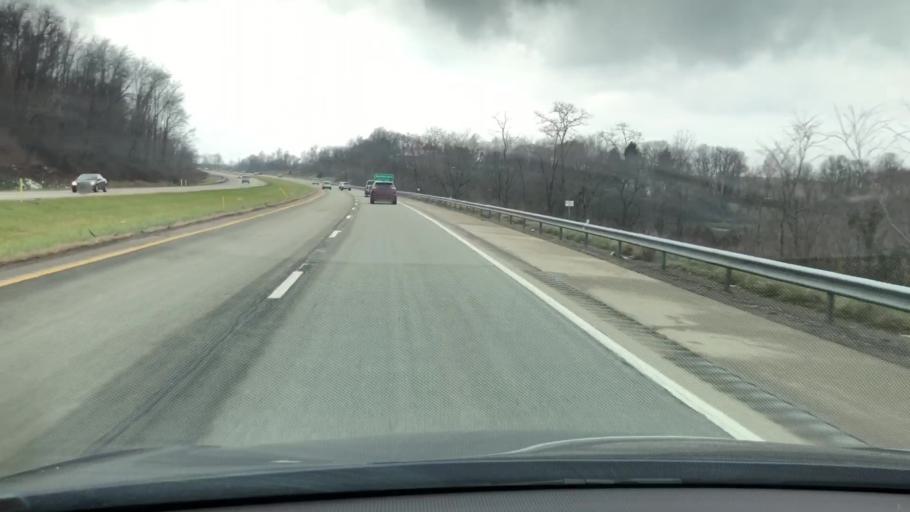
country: US
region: Pennsylvania
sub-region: Fayette County
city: Oliver
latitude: 39.9306
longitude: -79.6909
